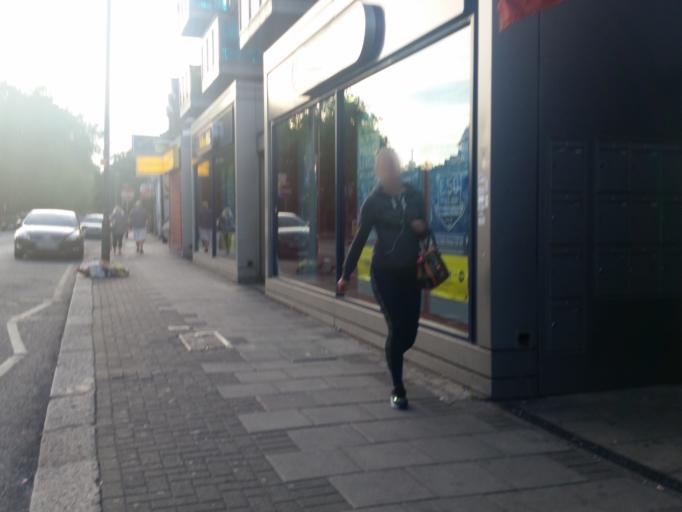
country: GB
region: England
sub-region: Greater London
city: Harringay
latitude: 51.5874
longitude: -0.0984
